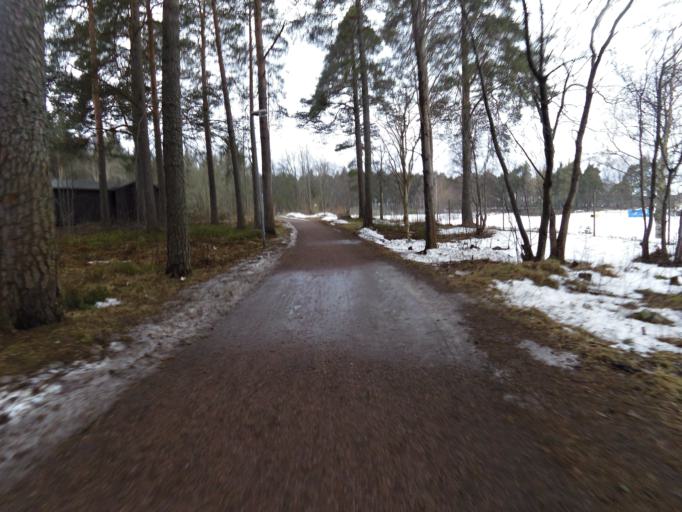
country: SE
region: Gaevleborg
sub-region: Gavle Kommun
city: Gavle
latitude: 60.6633
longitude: 17.1327
